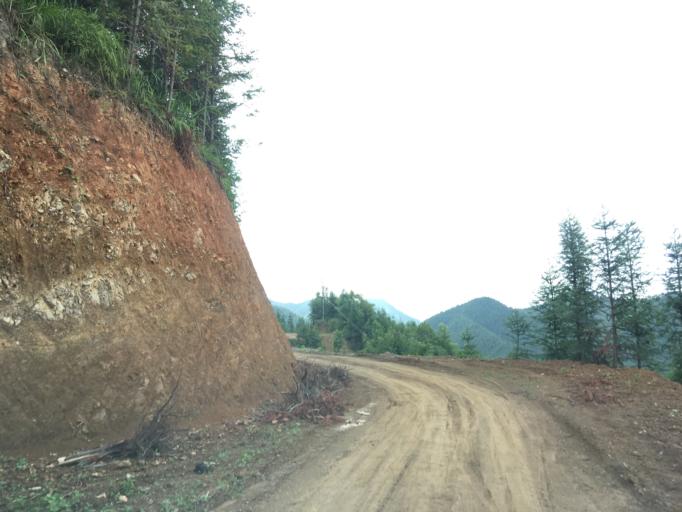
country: CN
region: Guangxi Zhuangzu Zizhiqu
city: Xinzhou
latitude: 24.8714
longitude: 105.8458
